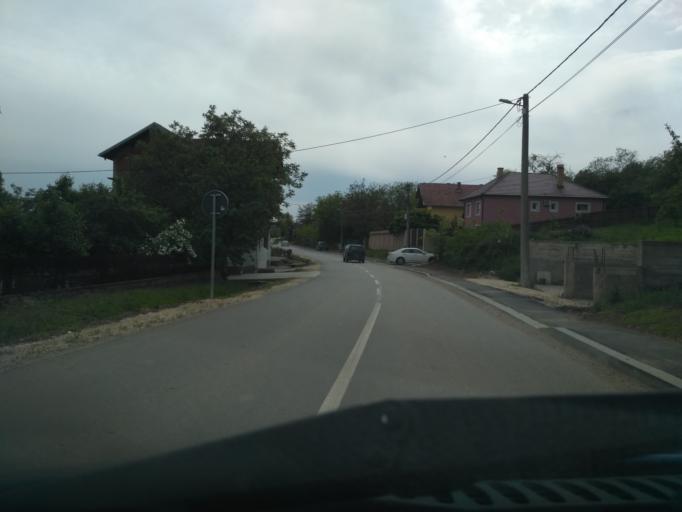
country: RS
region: Central Serbia
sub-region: Podunavski Okrug
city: Smederevska Palanka
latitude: 44.3598
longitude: 20.9824
